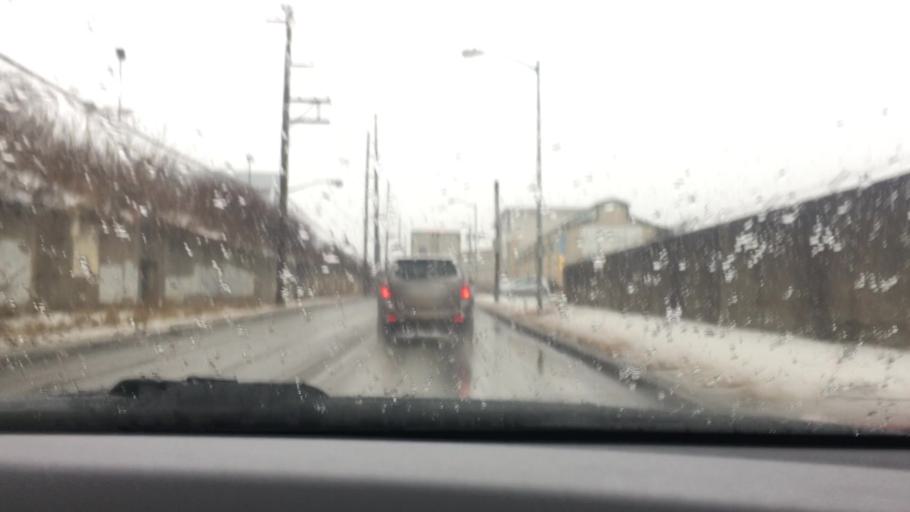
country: US
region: Pennsylvania
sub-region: Allegheny County
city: Mount Oliver
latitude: 40.4190
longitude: -79.9574
